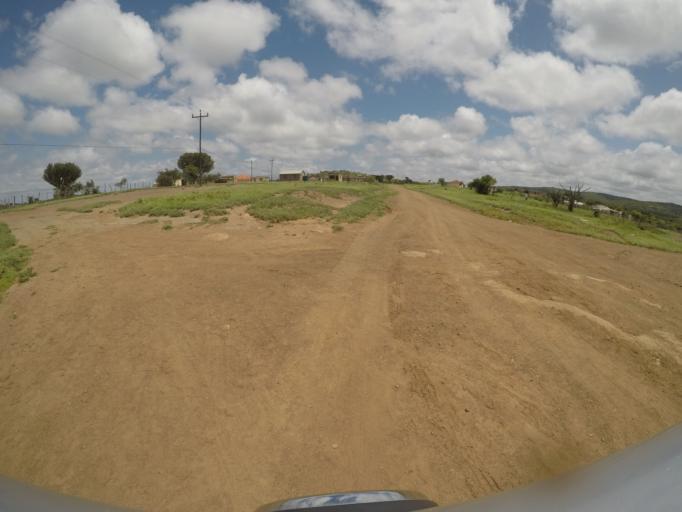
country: ZA
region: KwaZulu-Natal
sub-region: uThungulu District Municipality
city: Empangeni
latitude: -28.5766
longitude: 31.8387
